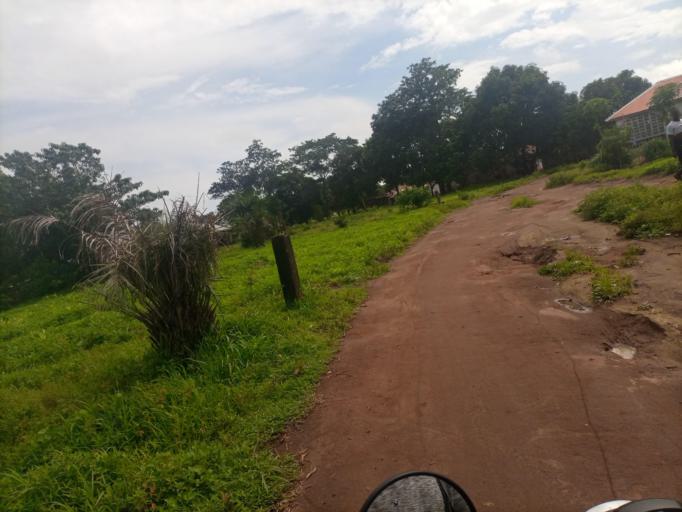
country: SL
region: Northern Province
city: Sawkta
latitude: 8.6352
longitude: -13.2096
